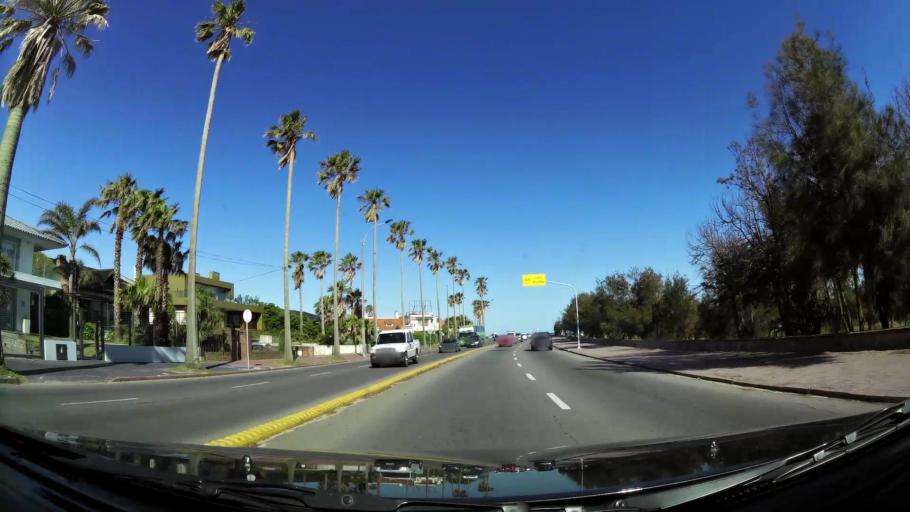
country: UY
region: Canelones
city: Paso de Carrasco
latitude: -34.8985
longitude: -56.0683
